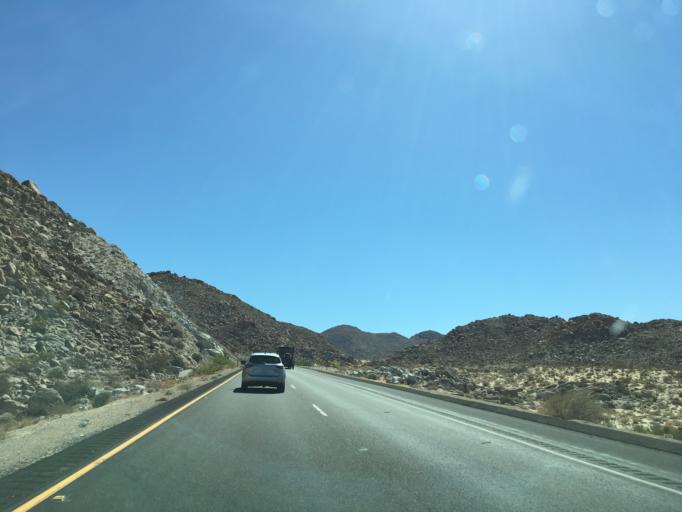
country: MX
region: Baja California
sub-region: Tecate
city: Cereso del Hongo
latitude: 32.7053
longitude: -116.0677
